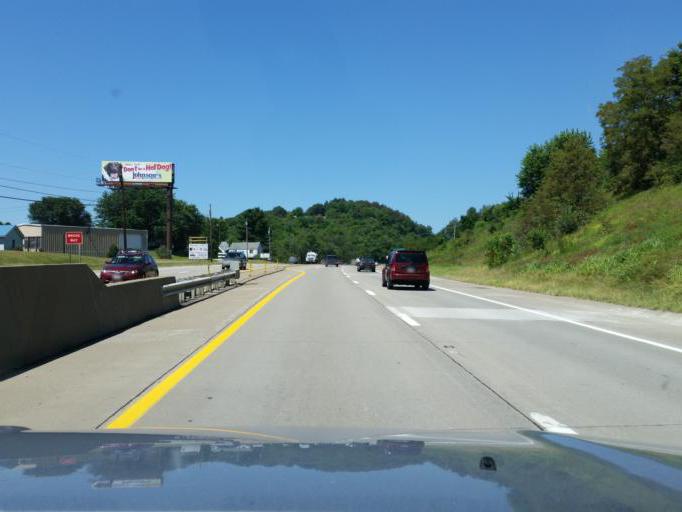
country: US
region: Pennsylvania
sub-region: Westmoreland County
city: Delmont
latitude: 40.3983
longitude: -79.5001
